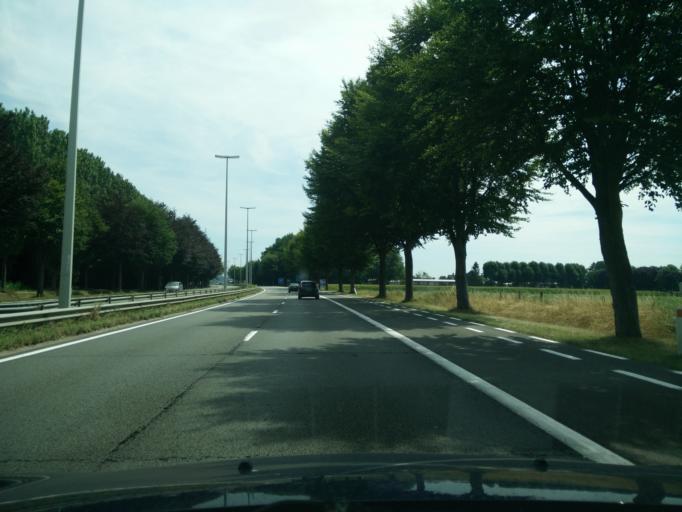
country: BE
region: Flanders
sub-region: Provincie Oost-Vlaanderen
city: Ninove
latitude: 50.8492
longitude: 4.0263
